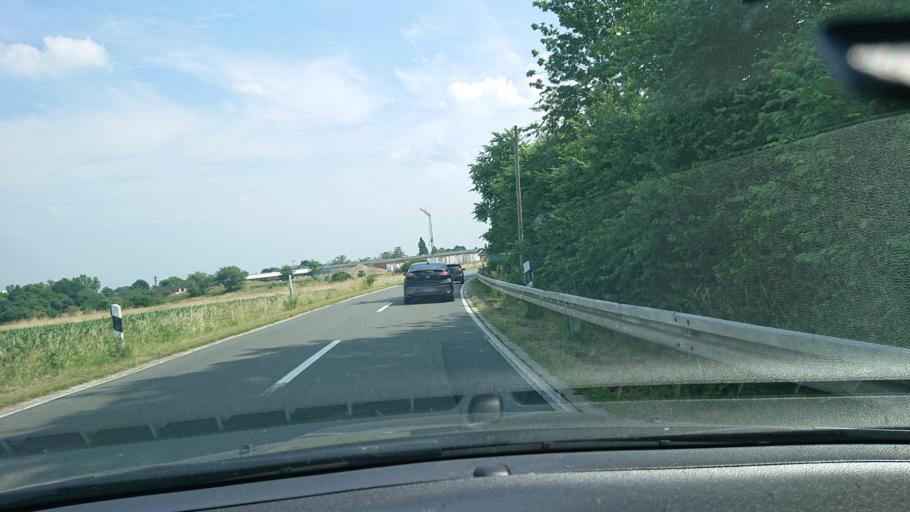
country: DE
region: North Rhine-Westphalia
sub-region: Regierungsbezirk Arnsberg
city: Soest
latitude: 51.5530
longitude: 8.0798
